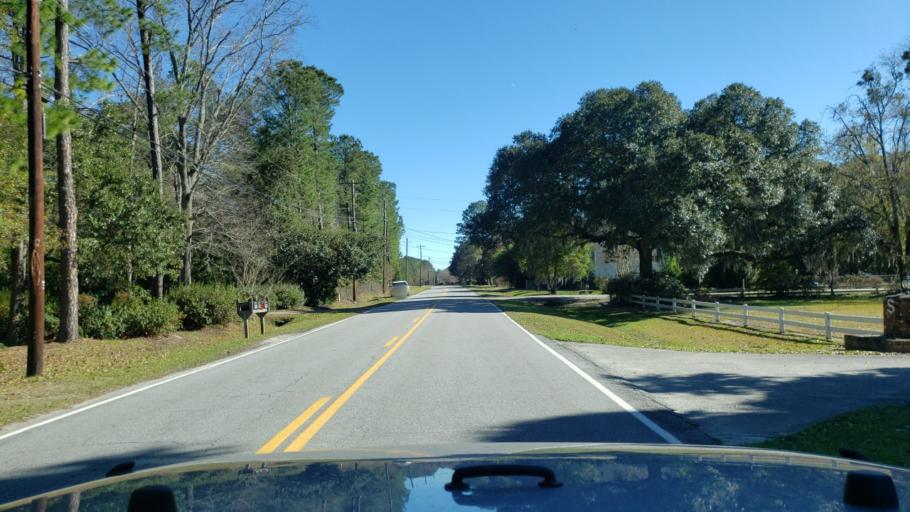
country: US
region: Georgia
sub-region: Chatham County
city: Georgetown
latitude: 32.0296
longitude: -81.1761
